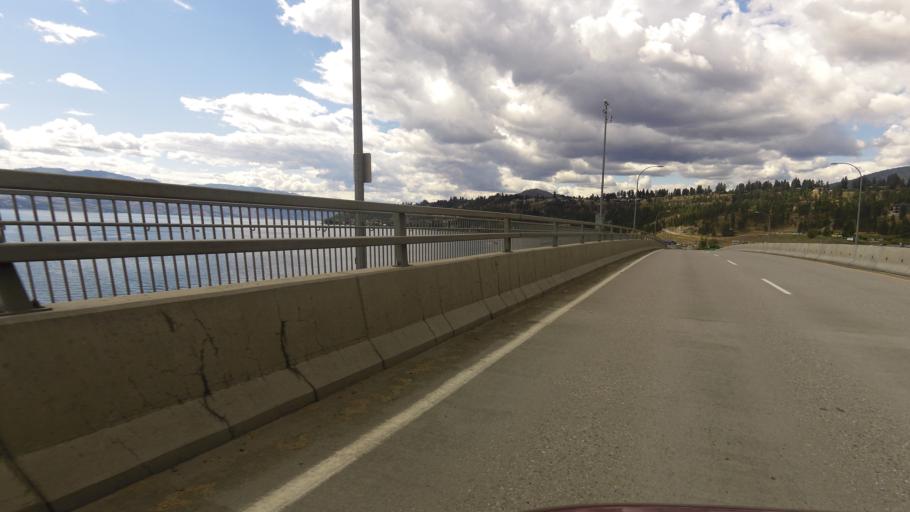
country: CA
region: British Columbia
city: Kelowna
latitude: 49.8786
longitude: -119.5170
